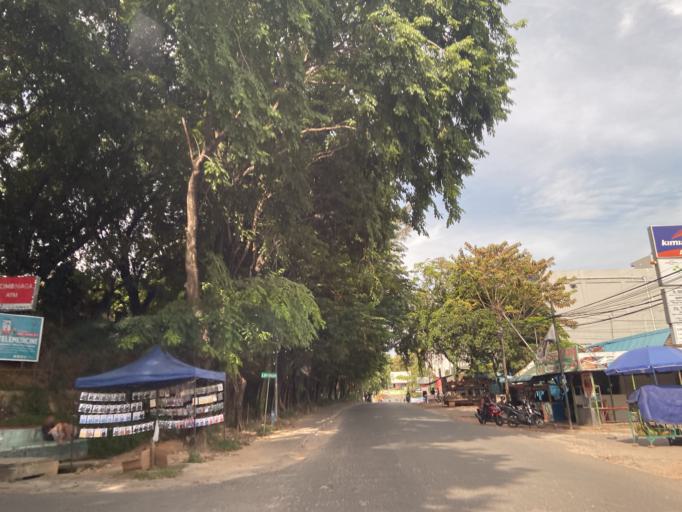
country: SG
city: Singapore
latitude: 1.1486
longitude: 104.0179
